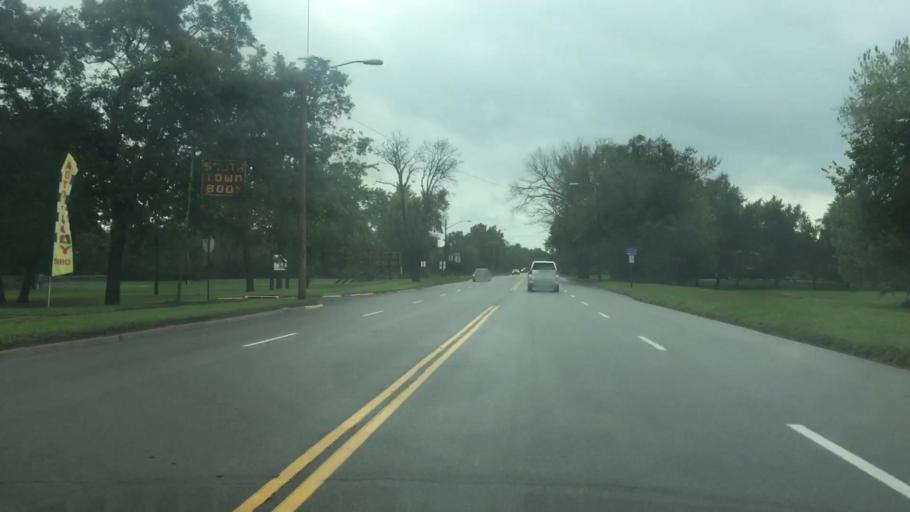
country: US
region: Kansas
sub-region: Allen County
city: Iola
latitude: 37.9161
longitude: -95.4091
